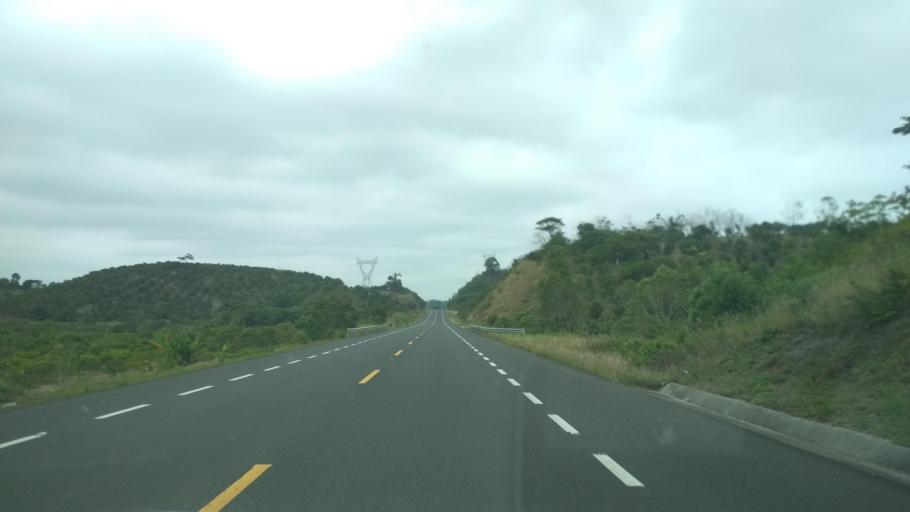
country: MX
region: Veracruz
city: Gutierrez Zamora
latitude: 20.3024
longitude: -97.0902
